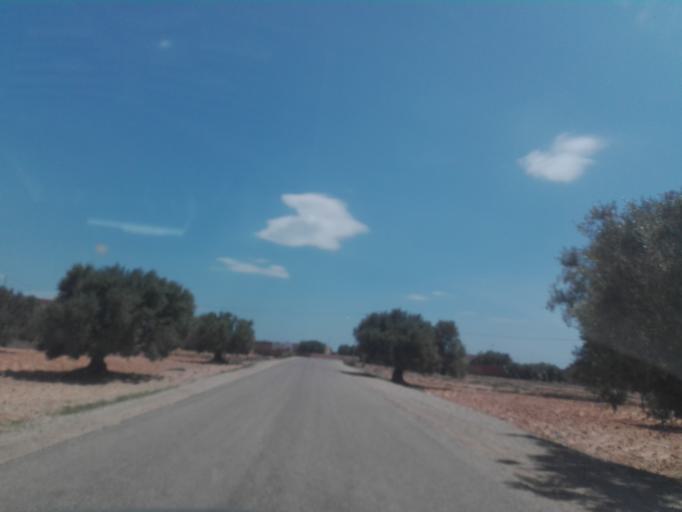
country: TN
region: Safaqis
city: Sfax
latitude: 34.6182
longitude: 10.6183
